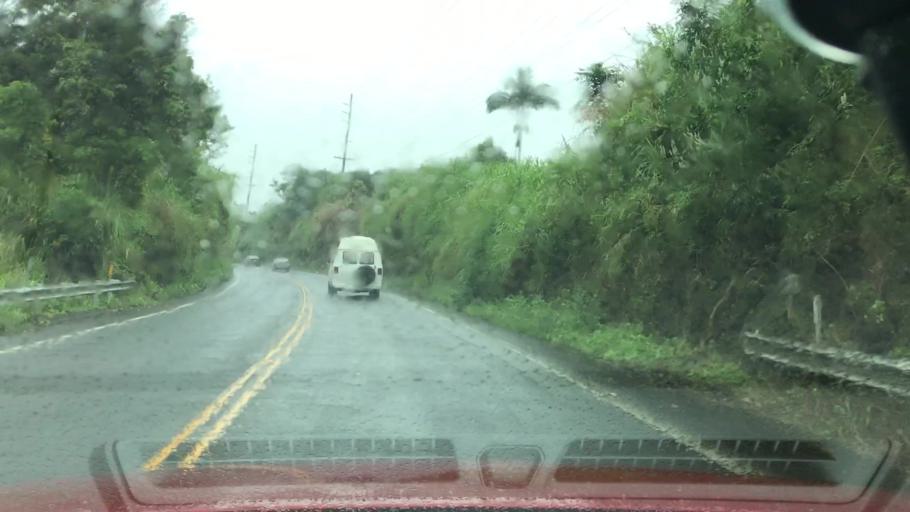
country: US
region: Hawaii
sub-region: Hawaii County
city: Pepeekeo
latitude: 19.9863
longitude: -155.2413
